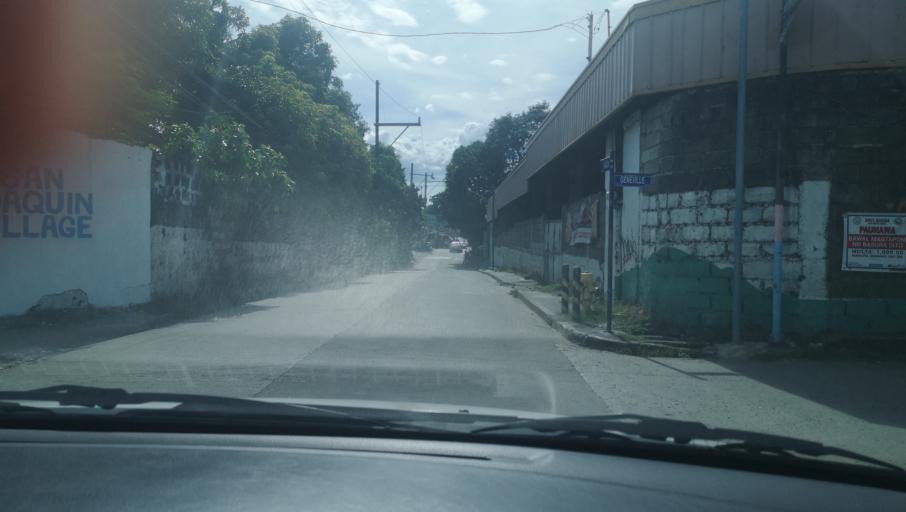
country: PH
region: Calabarzon
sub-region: Province of Rizal
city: San Mateo
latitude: 14.6746
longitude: 121.1115
